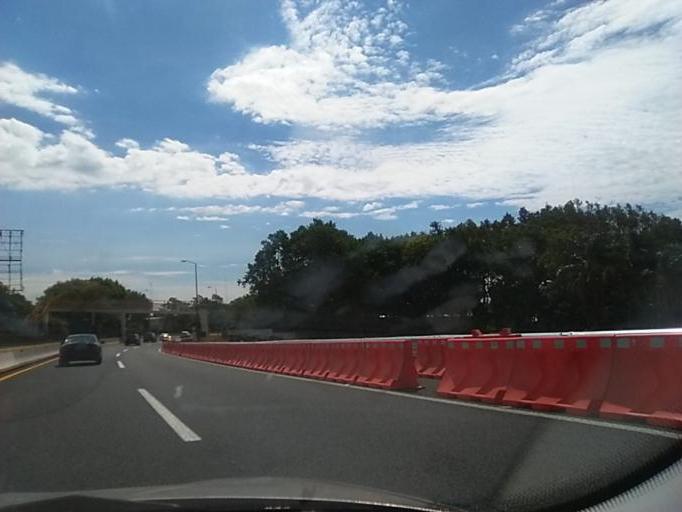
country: MX
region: Morelos
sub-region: Cuernavaca
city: Fraccionamiento Lomas de Ahuatlan
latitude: 18.9696
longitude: -99.2388
